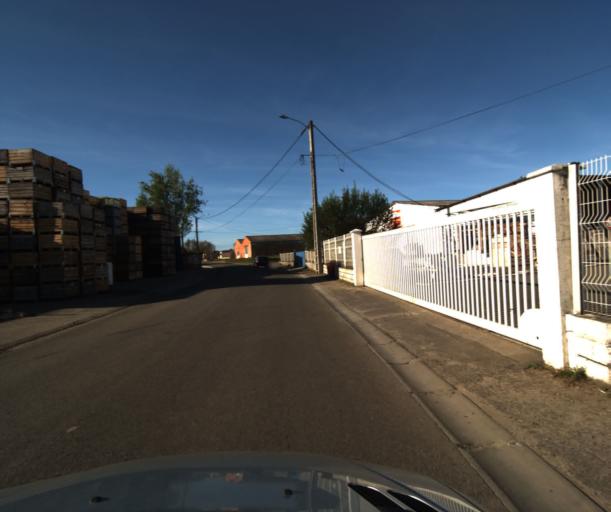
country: FR
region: Midi-Pyrenees
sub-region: Departement du Tarn-et-Garonne
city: Moissac
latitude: 44.1091
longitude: 1.1074
